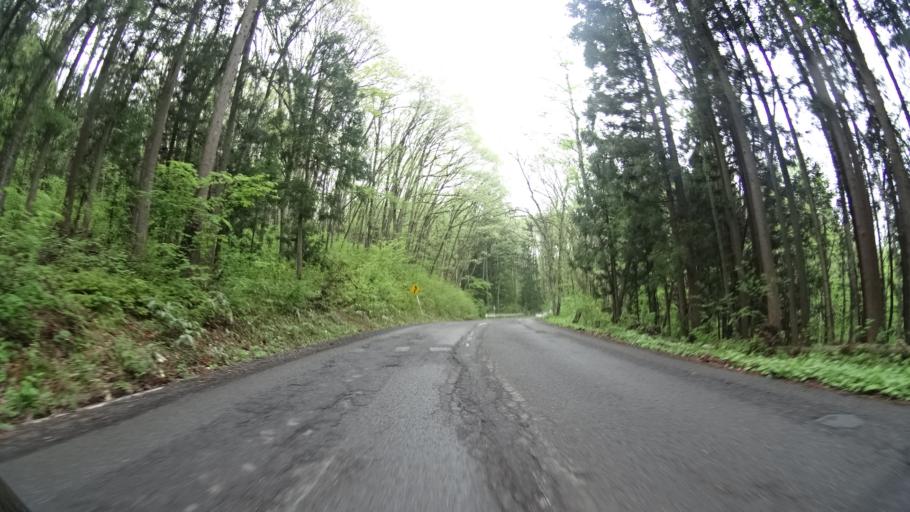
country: JP
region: Nagano
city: Nagano-shi
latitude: 36.7526
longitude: 138.2017
